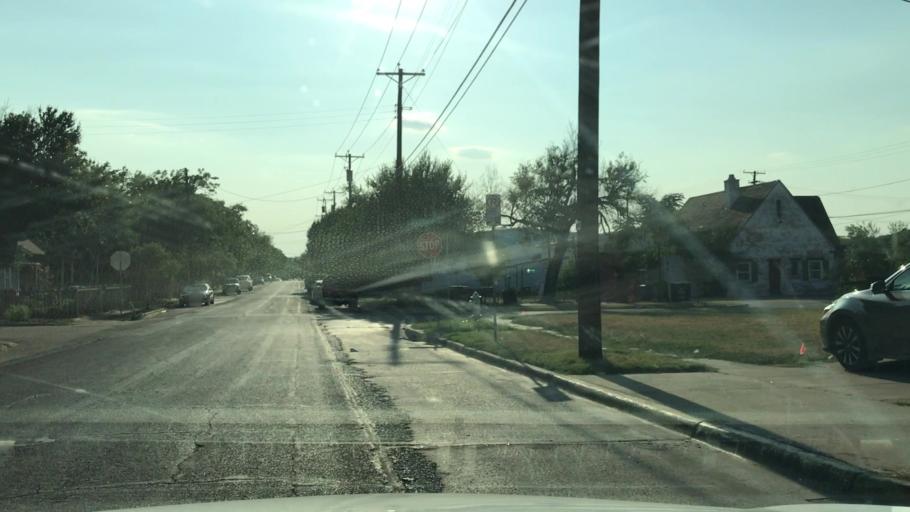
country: US
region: Texas
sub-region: Dallas County
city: Dallas
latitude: 32.7490
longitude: -96.8336
